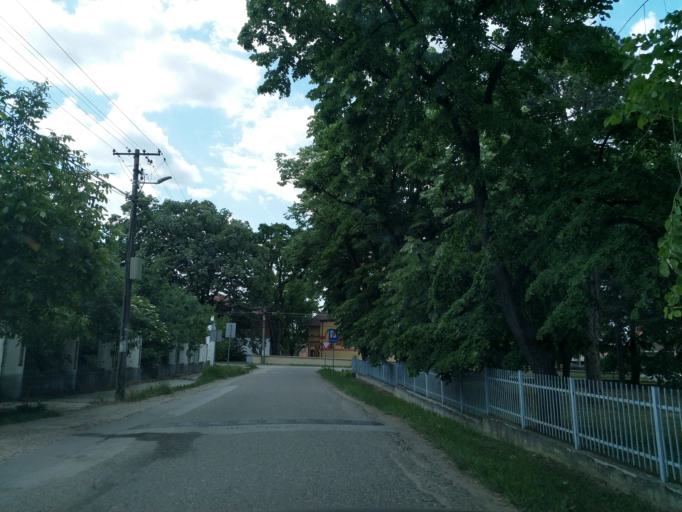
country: RS
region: Central Serbia
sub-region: Pomoravski Okrug
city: Jagodina
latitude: 43.9448
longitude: 21.2962
